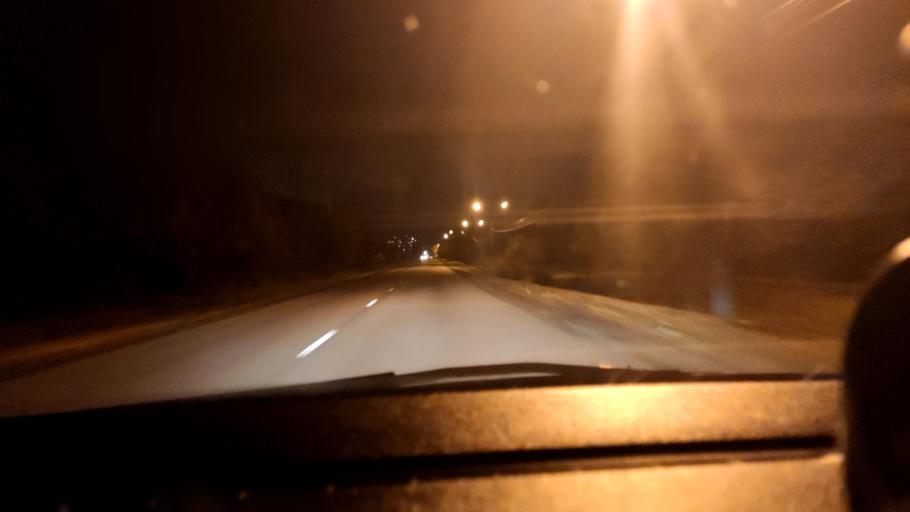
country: RU
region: Voronezj
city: Shilovo
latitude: 51.5564
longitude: 39.1019
